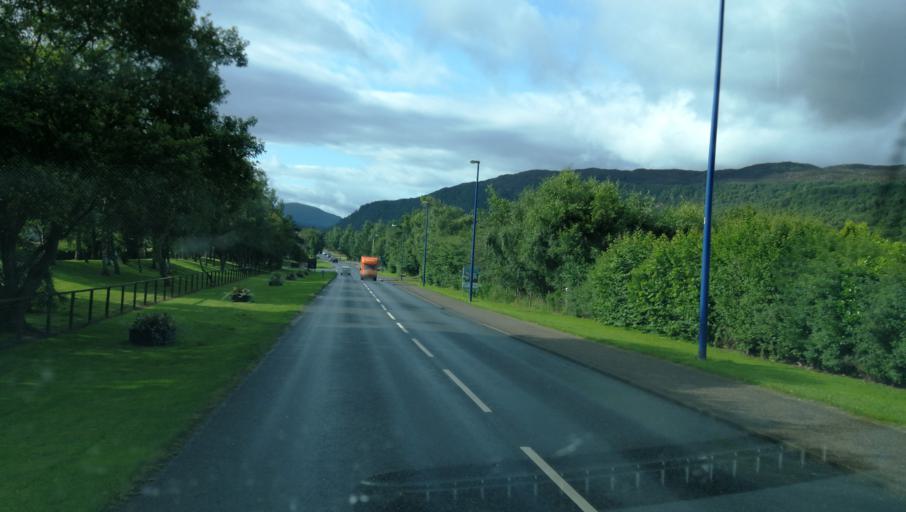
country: GB
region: Scotland
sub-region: Highland
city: Aviemore
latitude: 57.2021
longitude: -3.8275
